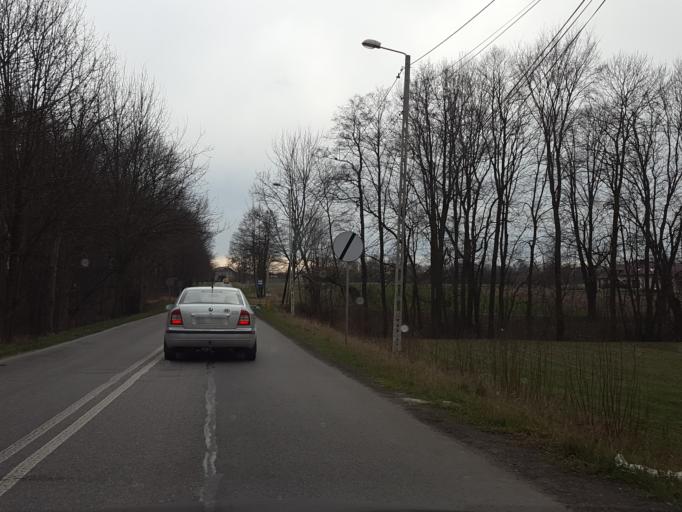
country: PL
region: Silesian Voivodeship
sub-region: Powiat gliwicki
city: Paniowki
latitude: 50.2057
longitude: 18.8103
